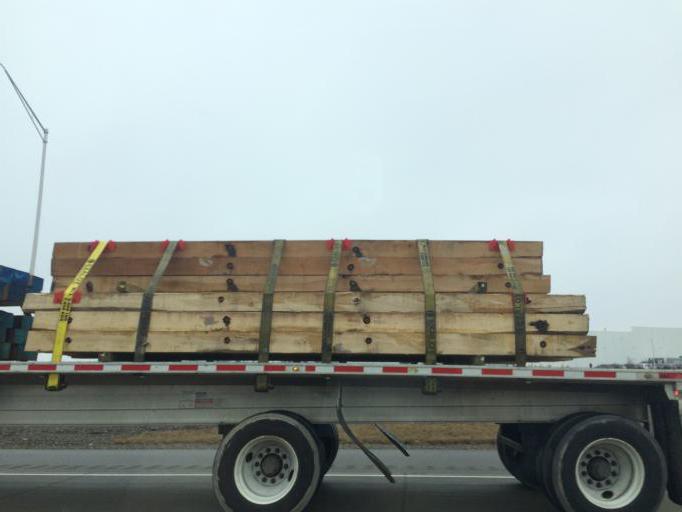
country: US
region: Illinois
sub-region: Kane County
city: Sleepy Hollow
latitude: 42.0822
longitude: -88.3387
